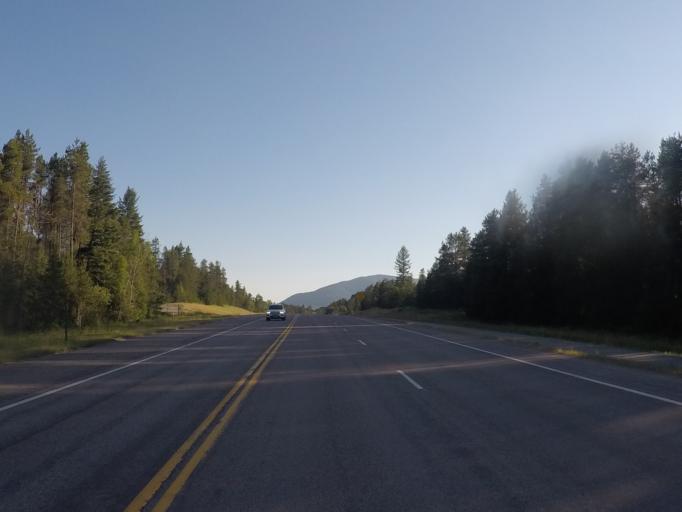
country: US
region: Montana
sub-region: Flathead County
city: Columbia Falls
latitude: 48.4585
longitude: -114.0085
